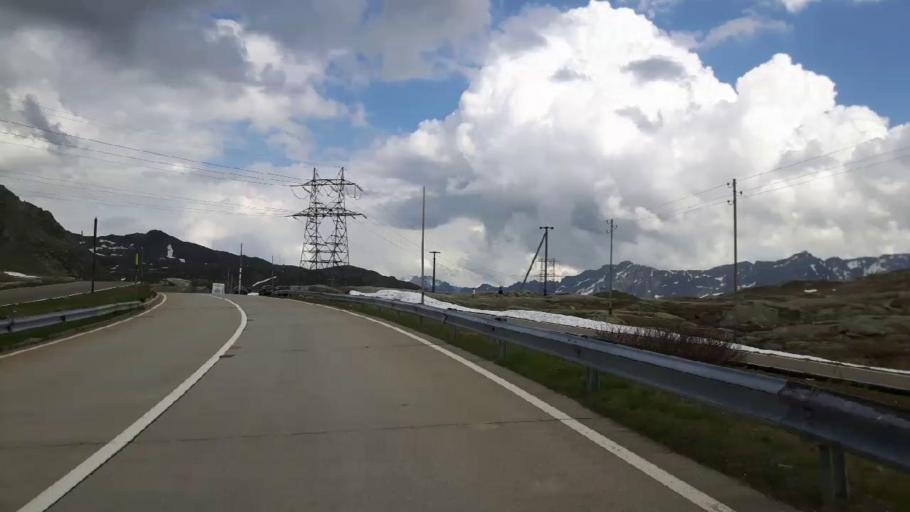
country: CH
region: Ticino
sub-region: Leventina District
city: Airolo
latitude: 46.5600
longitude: 8.5595
